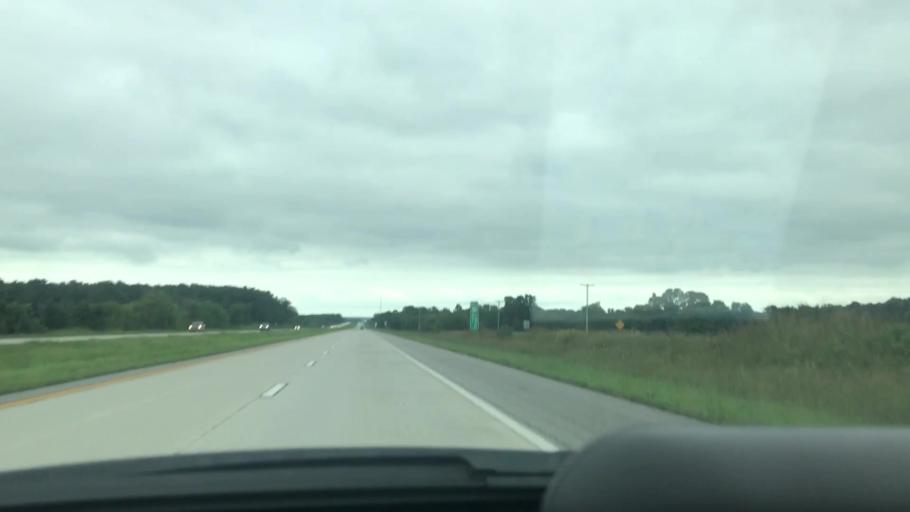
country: US
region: Missouri
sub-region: Greene County
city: Fair Grove
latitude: 37.4856
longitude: -93.1391
